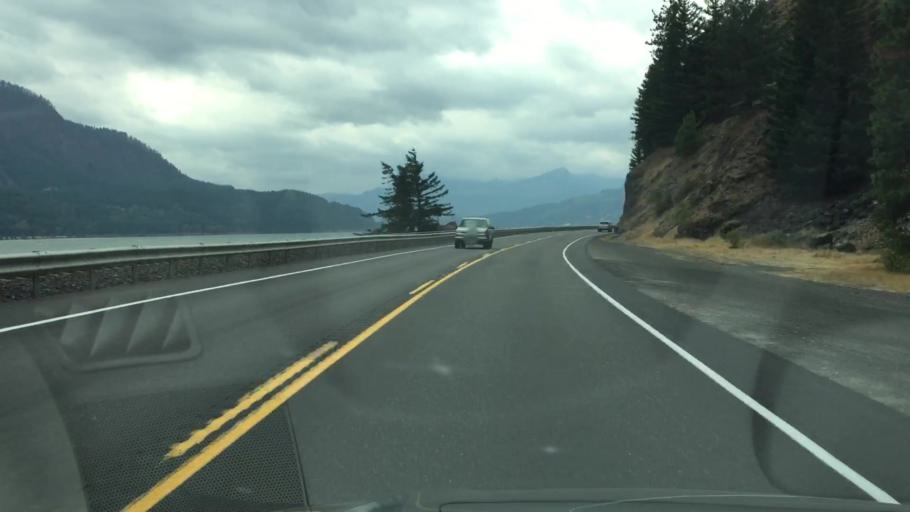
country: US
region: Washington
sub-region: Skamania County
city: Carson
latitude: 45.7026
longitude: -121.7556
